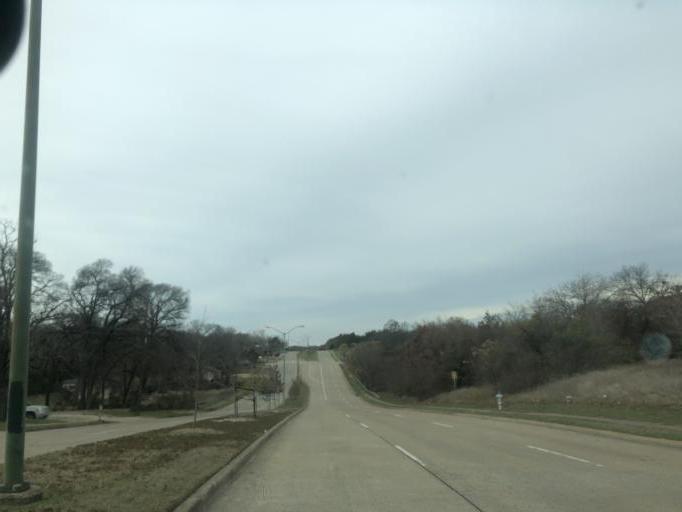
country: US
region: Texas
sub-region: Dallas County
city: Duncanville
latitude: 32.6749
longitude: -96.8267
